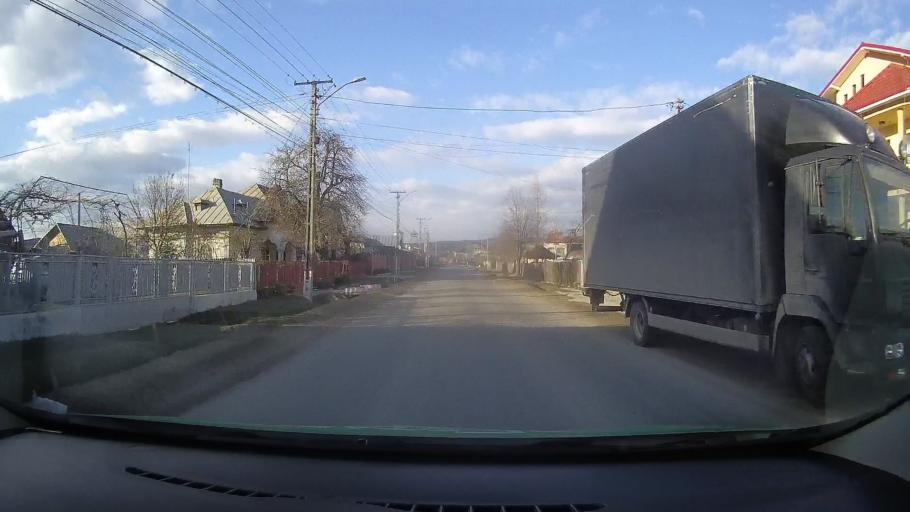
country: RO
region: Dambovita
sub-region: Comuna Ocnita
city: Ocnita
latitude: 44.9793
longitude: 25.5558
